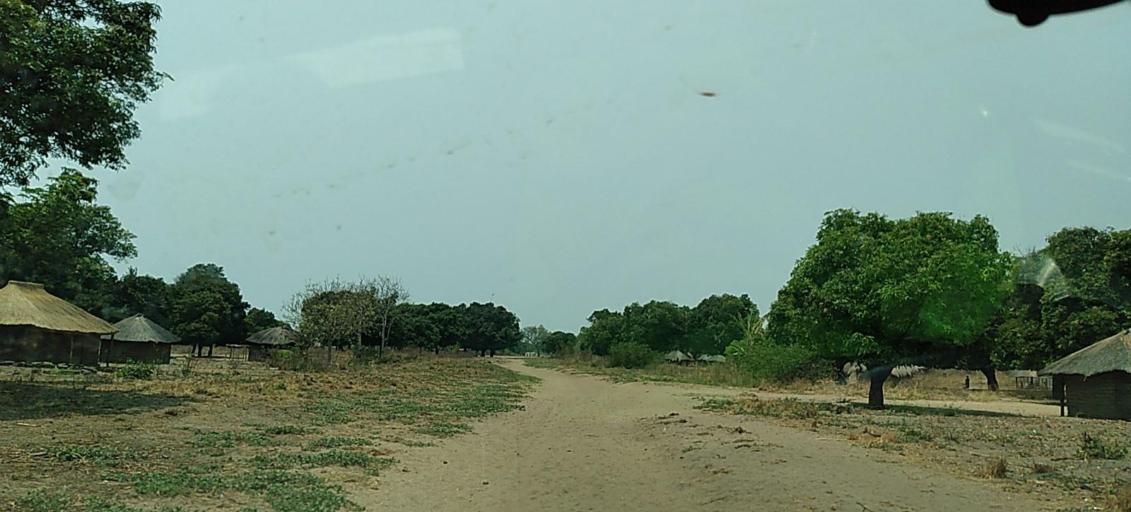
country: ZM
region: Western
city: Lukulu
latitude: -14.1591
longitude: 23.3146
